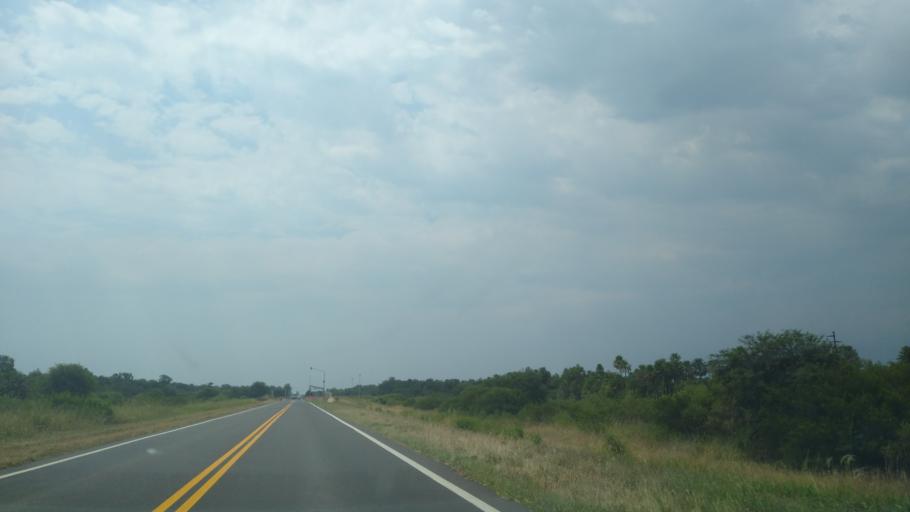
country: AR
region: Chaco
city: Margarita Belen
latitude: -27.1235
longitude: -58.9729
